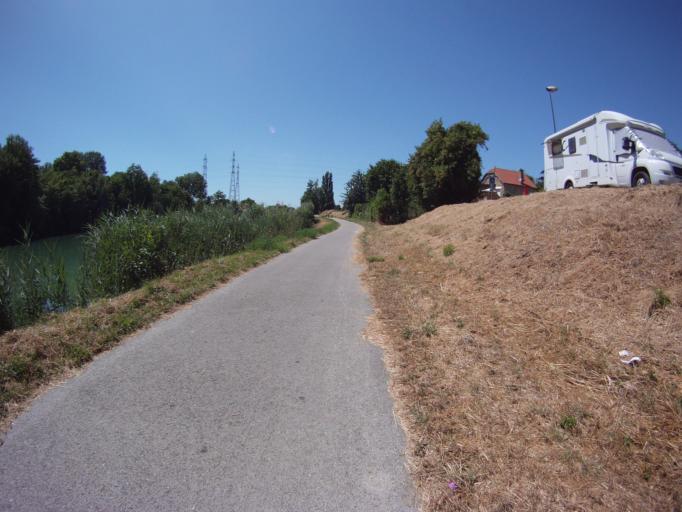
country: FR
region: Champagne-Ardenne
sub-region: Departement de la Marne
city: Damery
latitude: 49.0722
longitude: 3.8727
